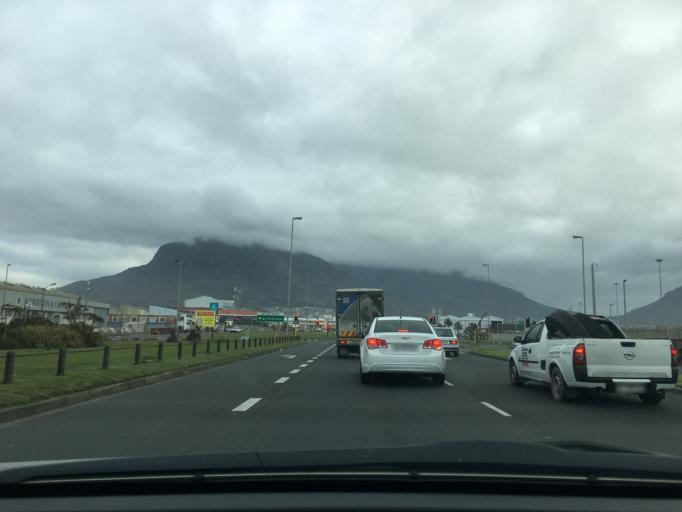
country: ZA
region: Western Cape
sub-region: City of Cape Town
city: Rosebank
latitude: -33.9122
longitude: 18.4681
